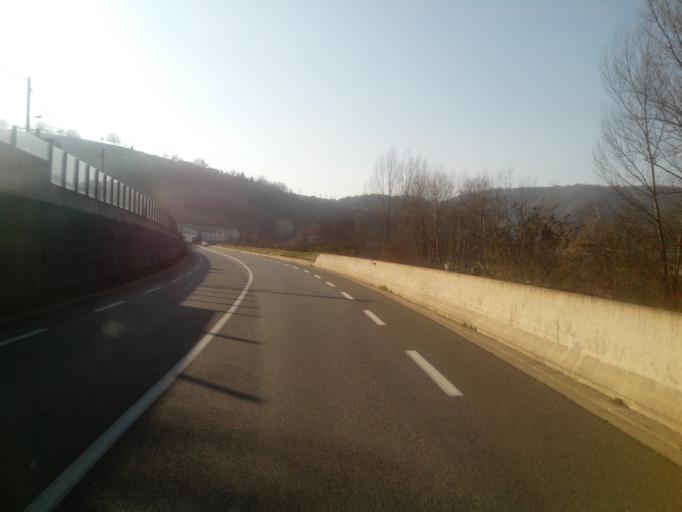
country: FR
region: Midi-Pyrenees
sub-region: Departement de l'Aveyron
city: Decazeville
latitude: 44.5618
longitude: 2.2411
